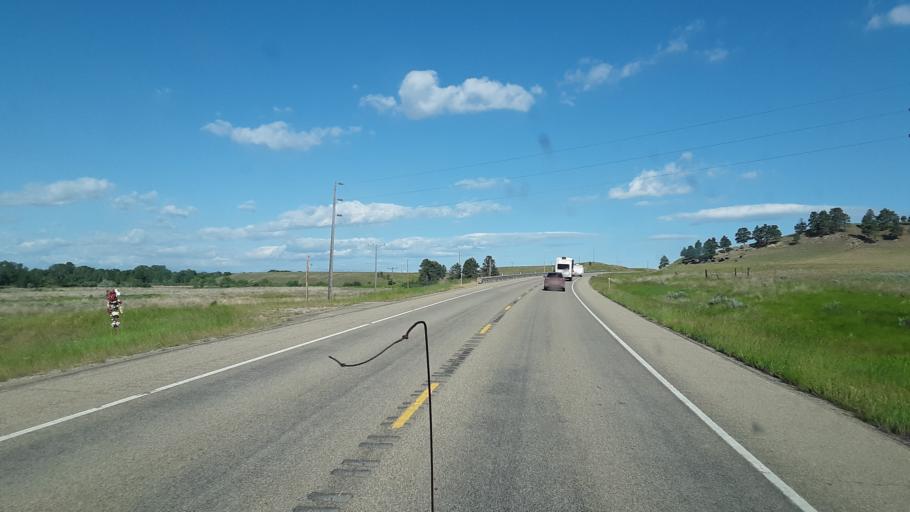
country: US
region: Montana
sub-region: Golden Valley County
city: Ryegate
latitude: 46.3196
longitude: -109.4320
